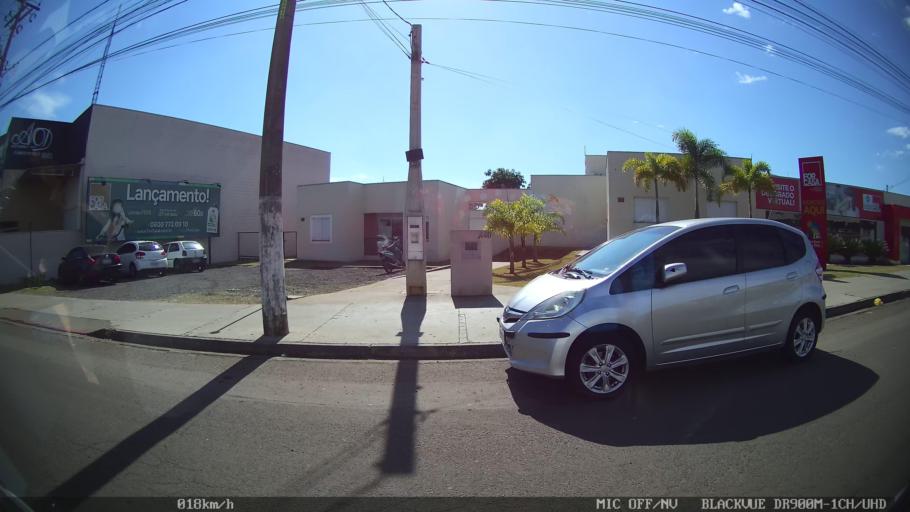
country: BR
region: Sao Paulo
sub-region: Santa Barbara D'Oeste
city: Santa Barbara d'Oeste
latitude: -22.7314
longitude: -47.3903
